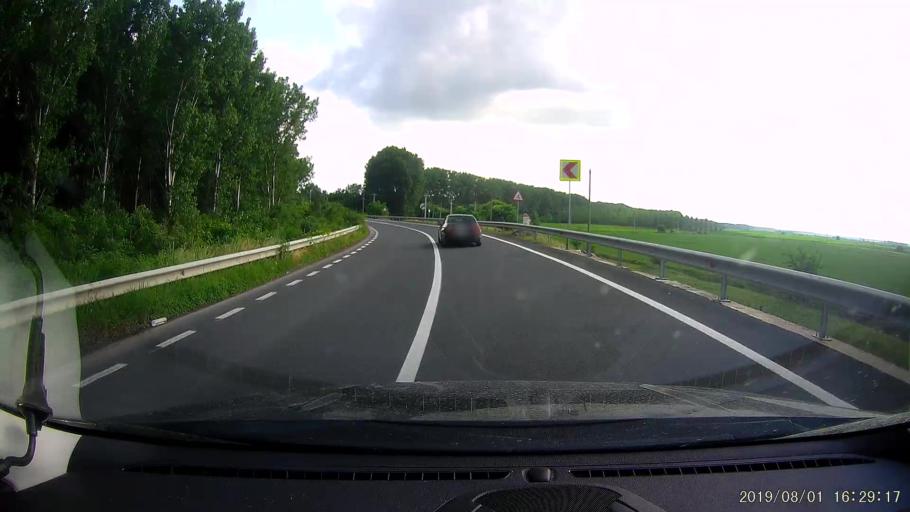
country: BG
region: Silistra
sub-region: Obshtina Silistra
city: Silistra
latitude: 44.1432
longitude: 27.2912
